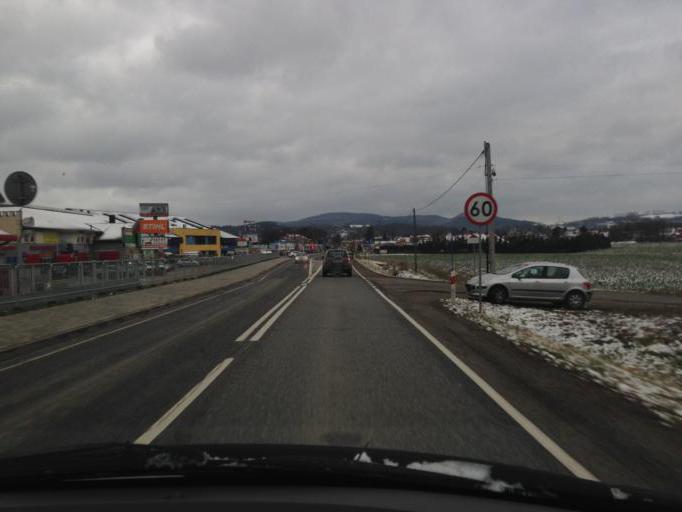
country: PL
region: Lesser Poland Voivodeship
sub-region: Powiat tarnowski
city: Zakliczyn
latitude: 49.8618
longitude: 20.8133
